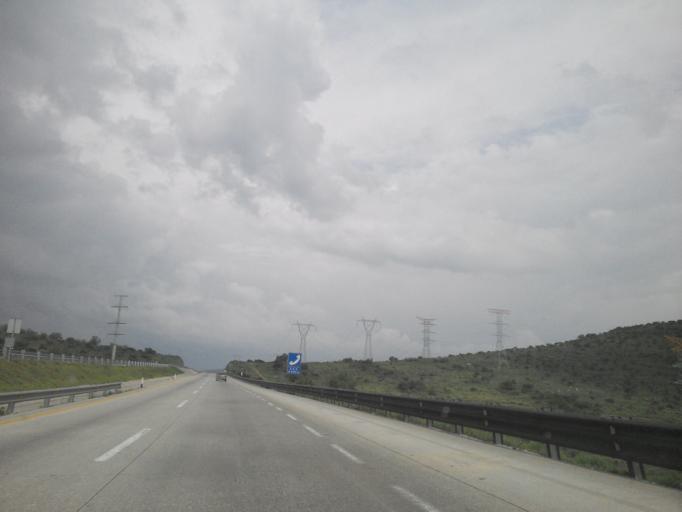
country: MX
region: Mexico
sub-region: Apaxco
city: Colonia Juarez
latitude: 20.0193
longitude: -99.1643
